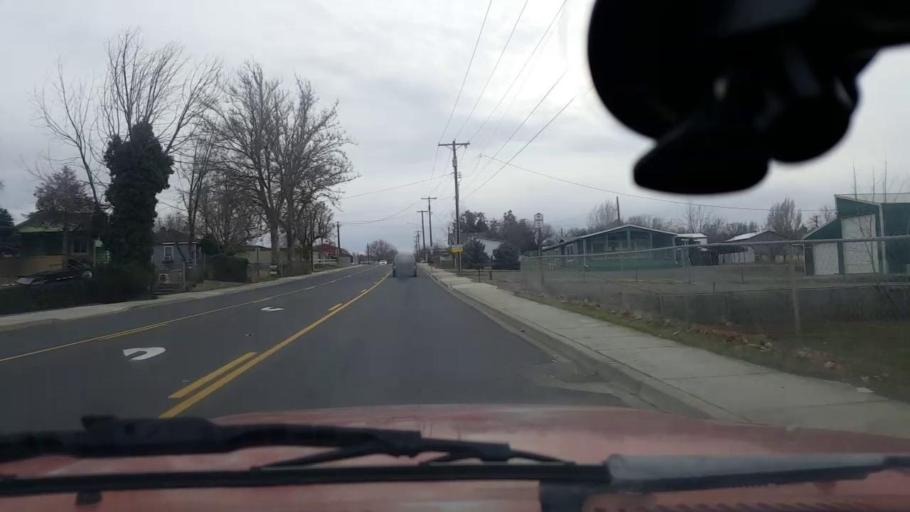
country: US
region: Washington
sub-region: Asotin County
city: West Clarkston-Highland
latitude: 46.4180
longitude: -117.0692
